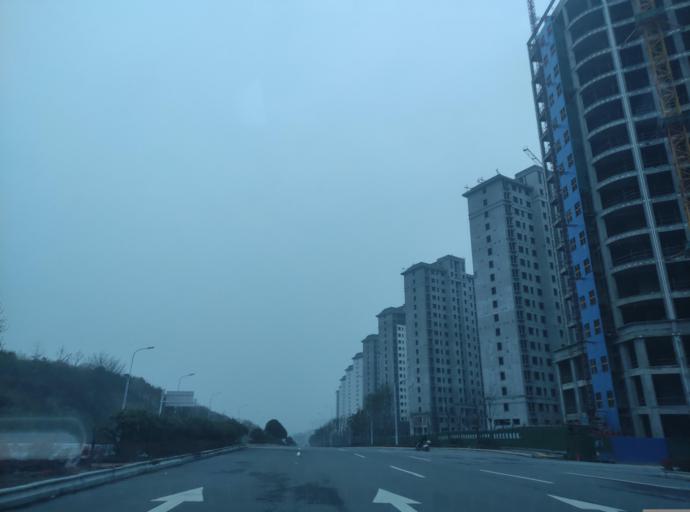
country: CN
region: Jiangxi Sheng
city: Pingxiang
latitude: 27.6681
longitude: 113.8445
